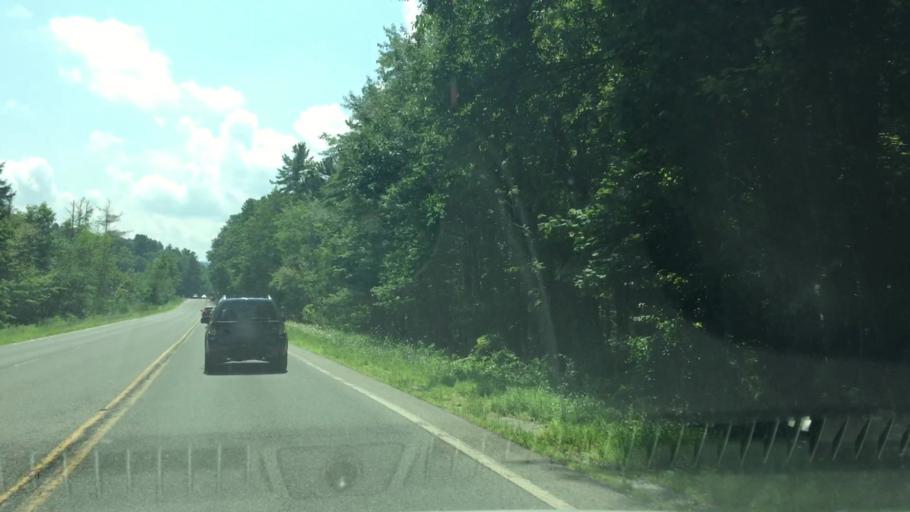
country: US
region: Massachusetts
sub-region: Berkshire County
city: Housatonic
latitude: 42.2307
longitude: -73.3400
